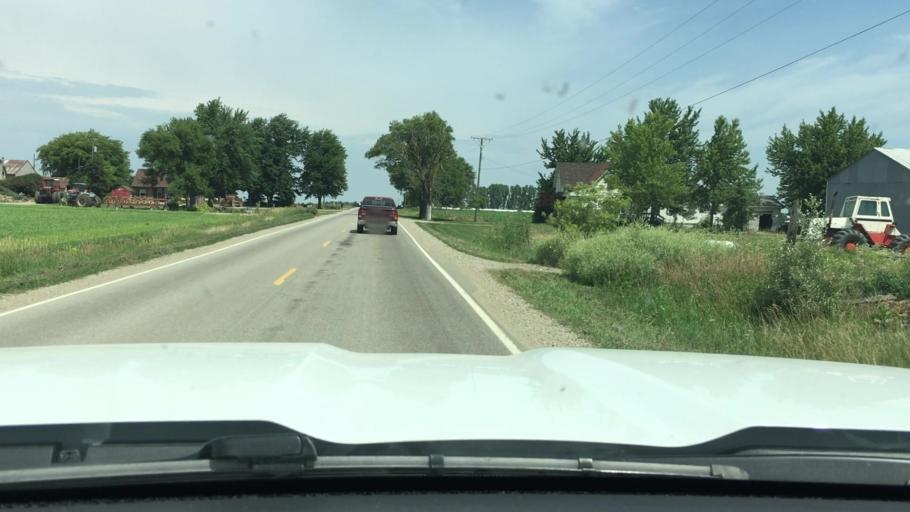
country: US
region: Michigan
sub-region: Sanilac County
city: Brown City
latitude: 43.2753
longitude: -82.9825
